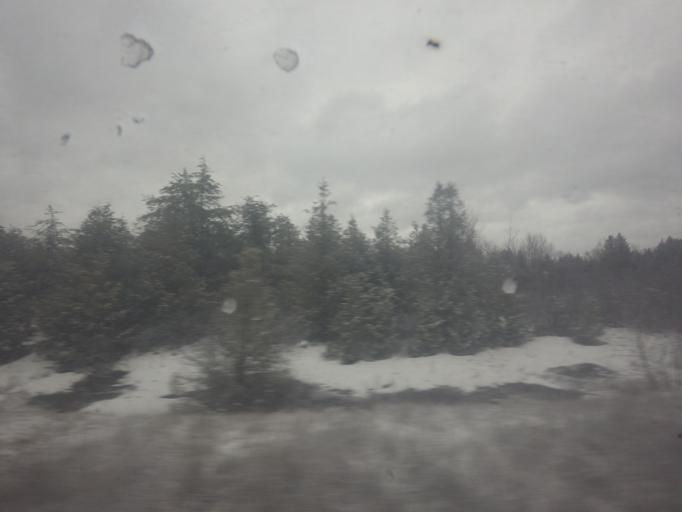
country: CA
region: Ontario
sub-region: Lanark County
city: Smiths Falls
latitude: 44.9593
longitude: -76.0036
